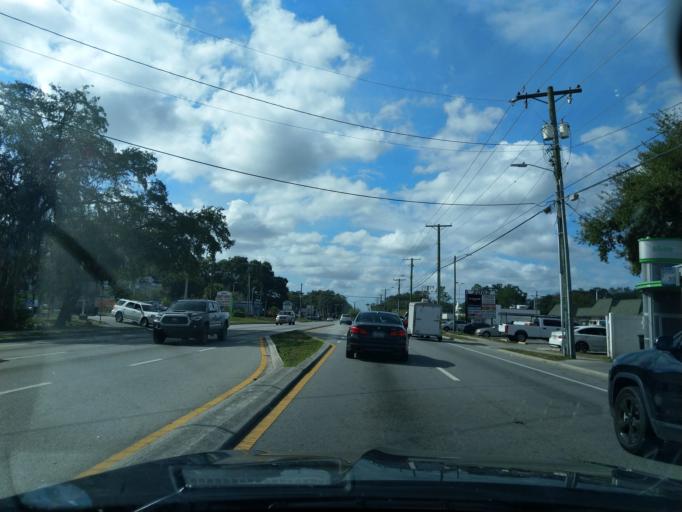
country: US
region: Florida
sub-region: Hillsborough County
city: University
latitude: 28.0693
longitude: -82.4355
